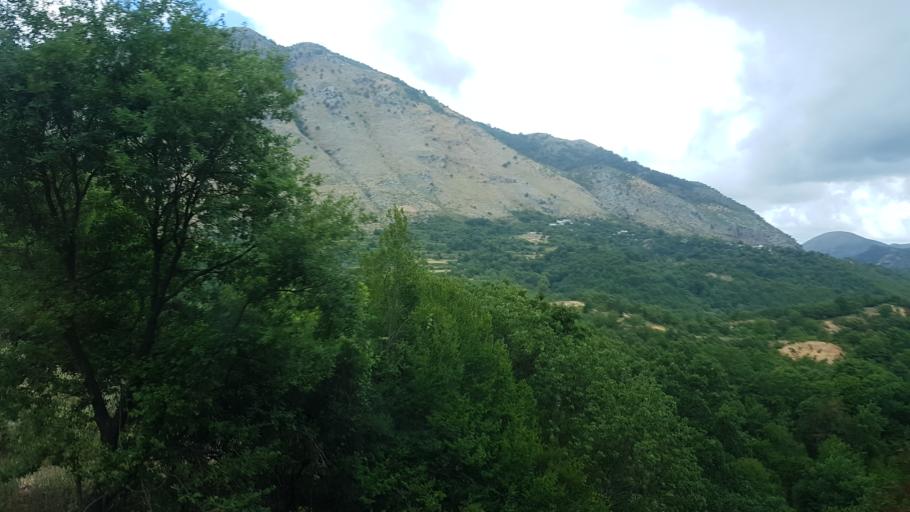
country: AL
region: Vlore
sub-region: Rrethi i Sarandes
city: Dhiver
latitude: 39.9141
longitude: 20.1923
